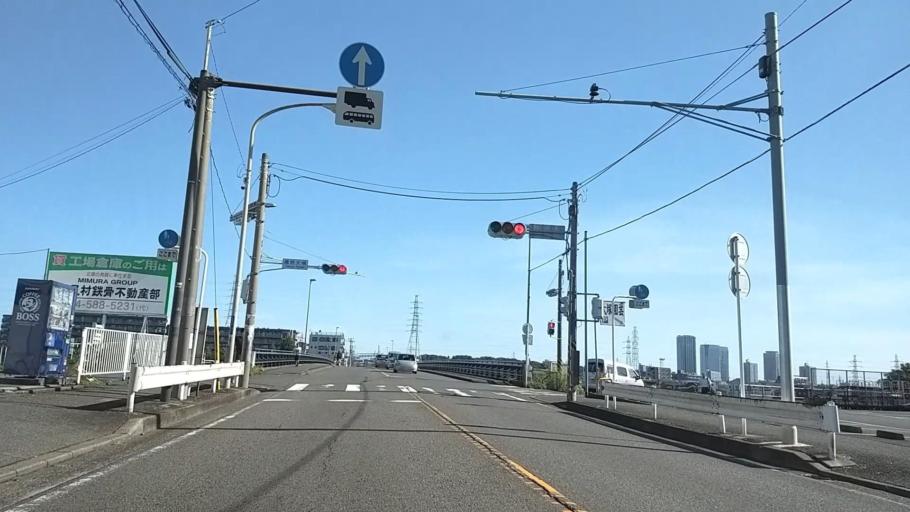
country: JP
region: Kanagawa
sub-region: Kawasaki-shi
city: Kawasaki
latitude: 35.5373
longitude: 139.6547
